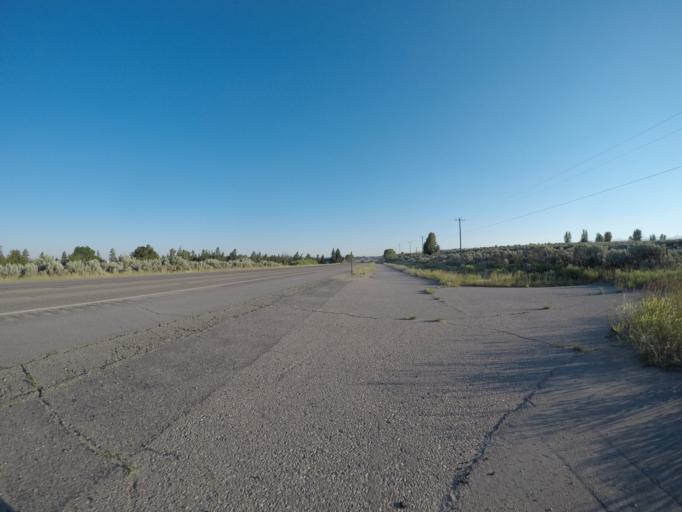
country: US
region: Wyoming
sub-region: Sublette County
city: Pinedale
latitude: 42.8469
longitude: -109.8483
